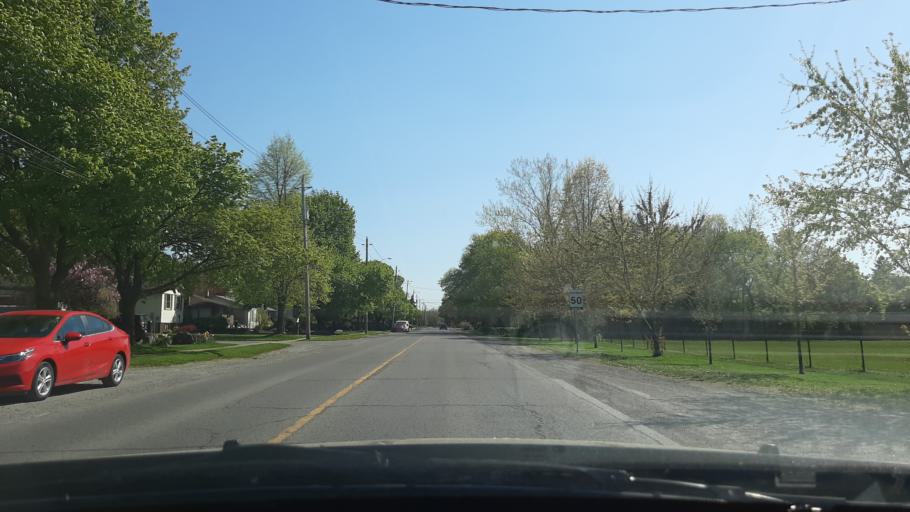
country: CA
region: Ontario
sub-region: Regional Municipality of Niagara
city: St. Catharines
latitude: 43.1994
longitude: -79.2233
